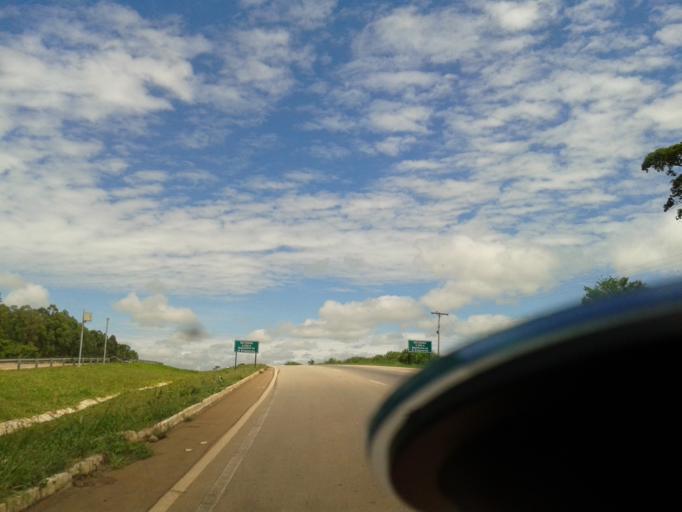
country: BR
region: Goias
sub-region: Inhumas
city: Inhumas
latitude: -16.3115
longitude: -49.5252
